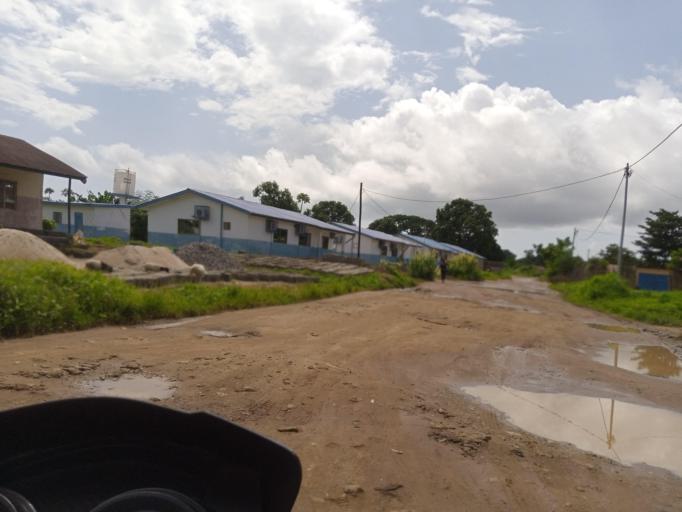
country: SL
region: Northern Province
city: Tintafor
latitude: 8.6242
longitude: -13.2125
